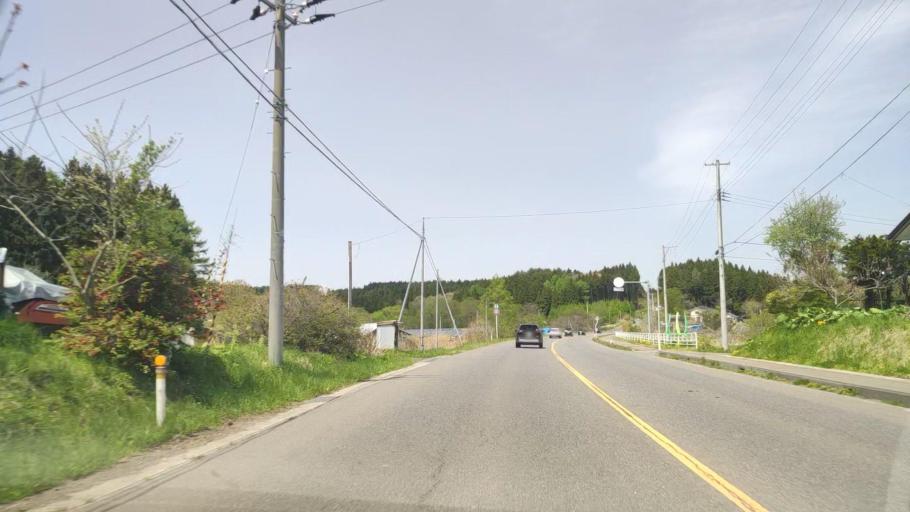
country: JP
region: Aomori
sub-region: Misawa Shi
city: Inuotose
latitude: 40.5617
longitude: 141.3832
